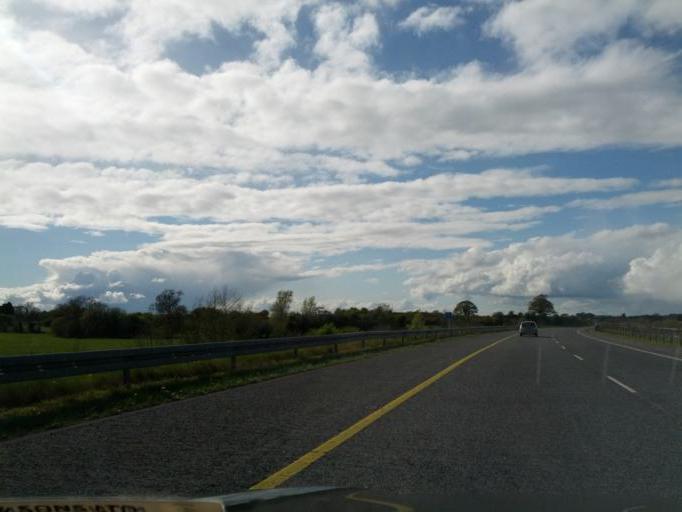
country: IE
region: Leinster
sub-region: An Mhi
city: Longwood
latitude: 53.4278
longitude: -6.9878
